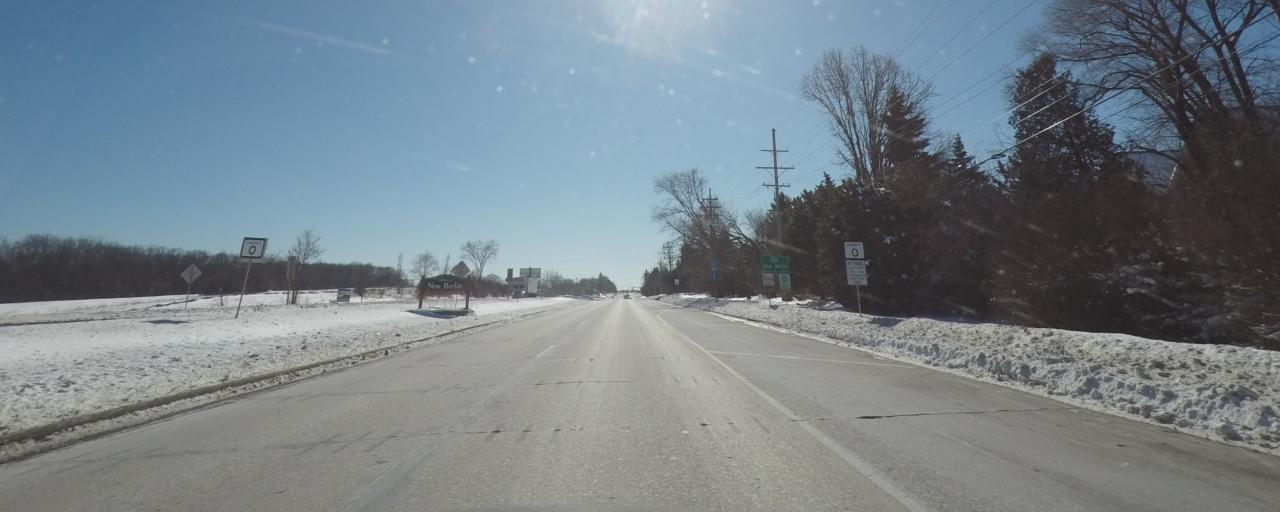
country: US
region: Wisconsin
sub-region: Waukesha County
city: New Berlin
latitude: 43.0150
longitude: -88.1073
